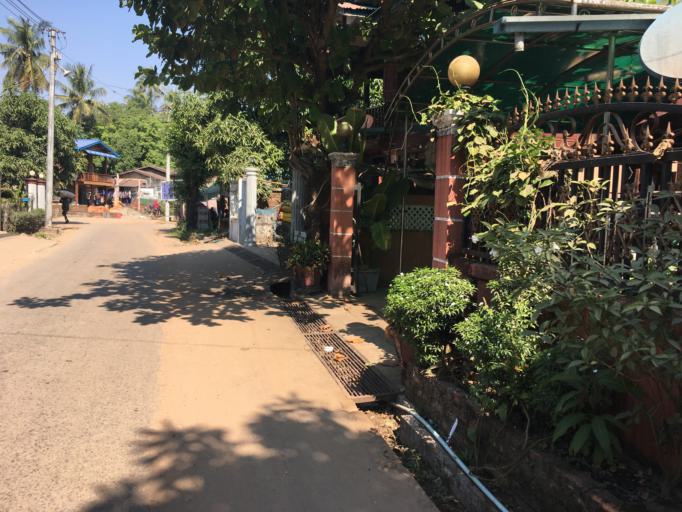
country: MM
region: Mon
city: Mawlamyine
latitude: 16.4340
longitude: 97.7054
